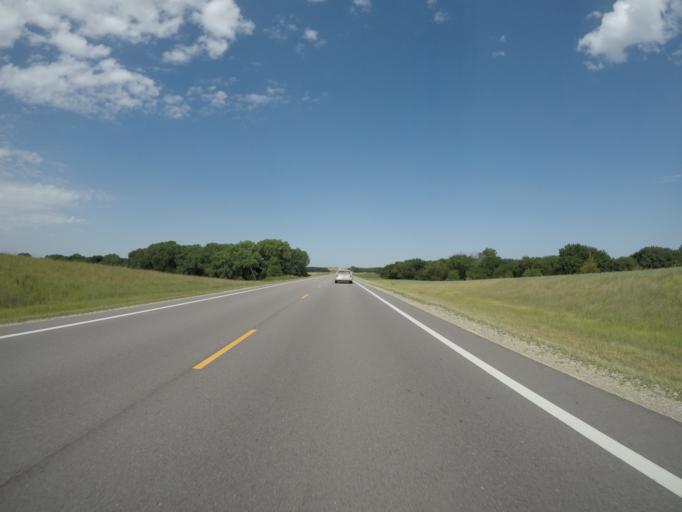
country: US
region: Kansas
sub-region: Clay County
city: Clay Center
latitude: 39.3788
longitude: -97.3025
